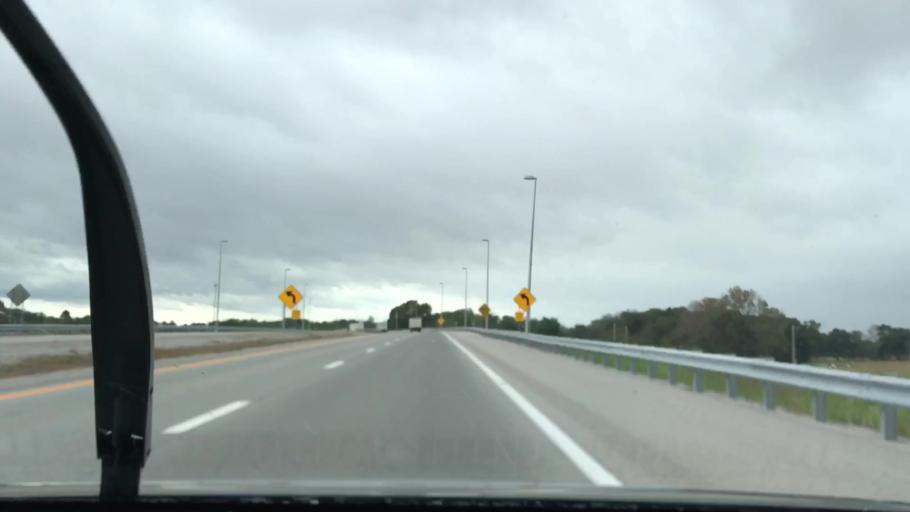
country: US
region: Kentucky
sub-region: Christian County
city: Fort Campbell North
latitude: 36.7465
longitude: -87.5104
